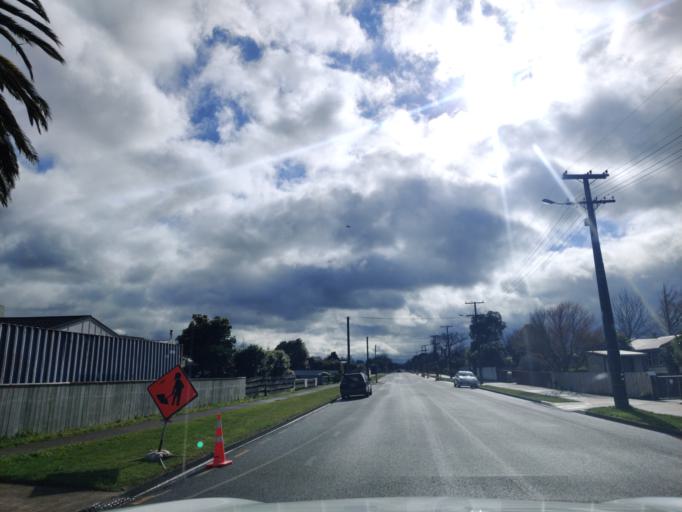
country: NZ
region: Manawatu-Wanganui
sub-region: Palmerston North City
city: Palmerston North
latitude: -40.2892
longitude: 175.7582
